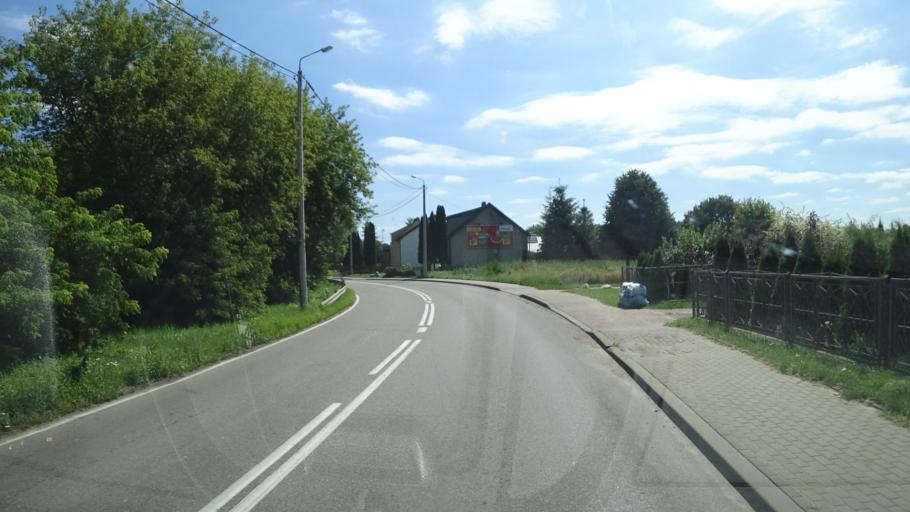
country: PL
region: Warmian-Masurian Voivodeship
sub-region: Powiat elcki
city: Prostki
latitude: 53.6882
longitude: 22.4498
